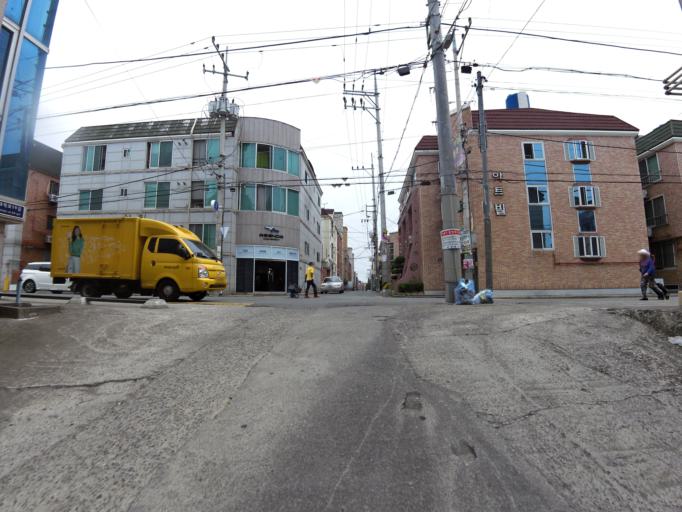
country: KR
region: Gyeongsangbuk-do
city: Gyeongsan-si
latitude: 35.8392
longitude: 128.7520
